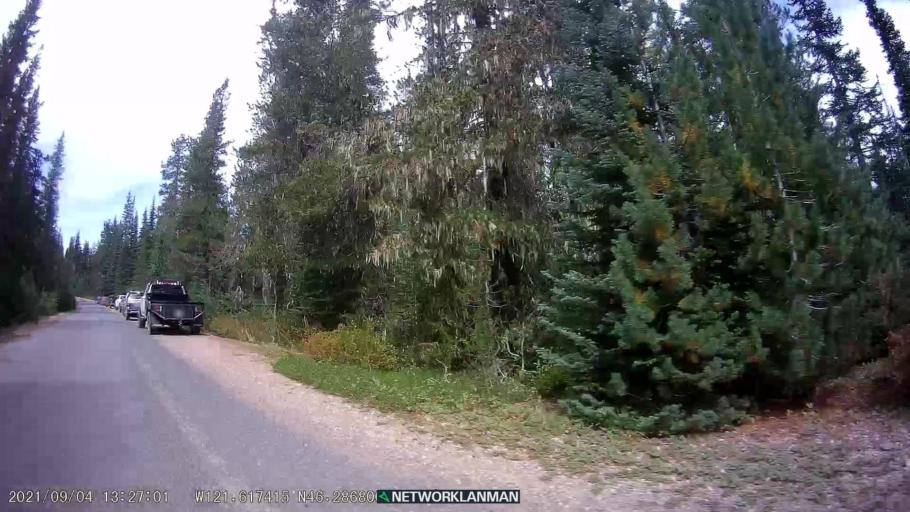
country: US
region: Washington
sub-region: Klickitat County
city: White Salmon
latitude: 46.2871
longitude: -121.6178
